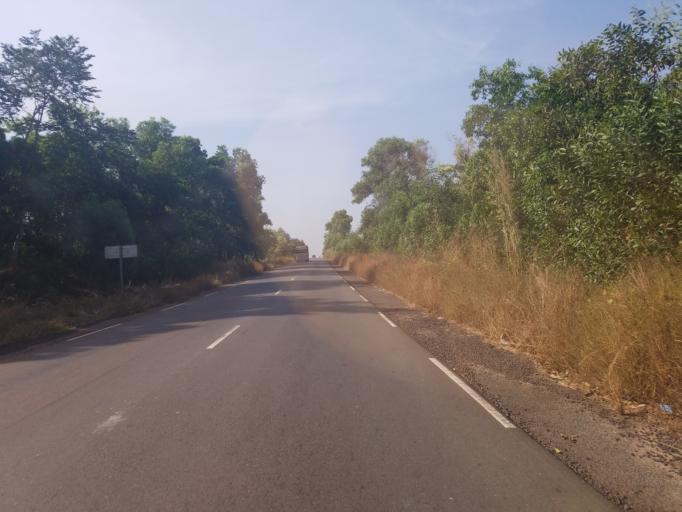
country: GN
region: Boke
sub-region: Boffa
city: Boffa
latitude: 10.1987
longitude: -14.0615
